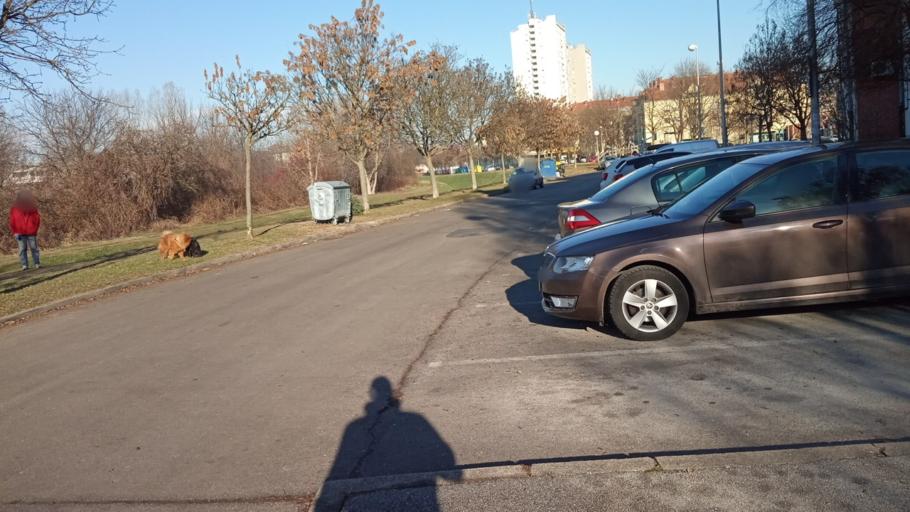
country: HR
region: Grad Zagreb
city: Jankomir
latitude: 45.7855
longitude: 15.9390
